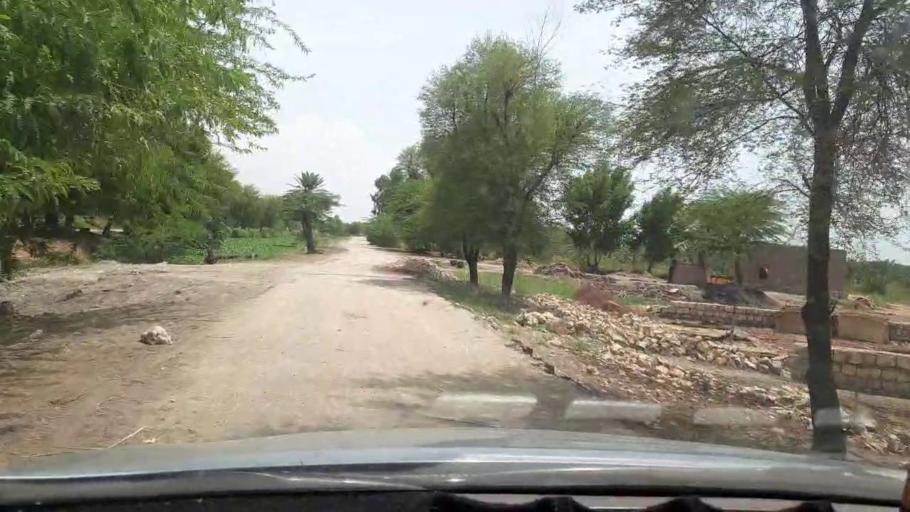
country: PK
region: Sindh
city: Khairpur
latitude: 27.4696
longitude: 68.7971
